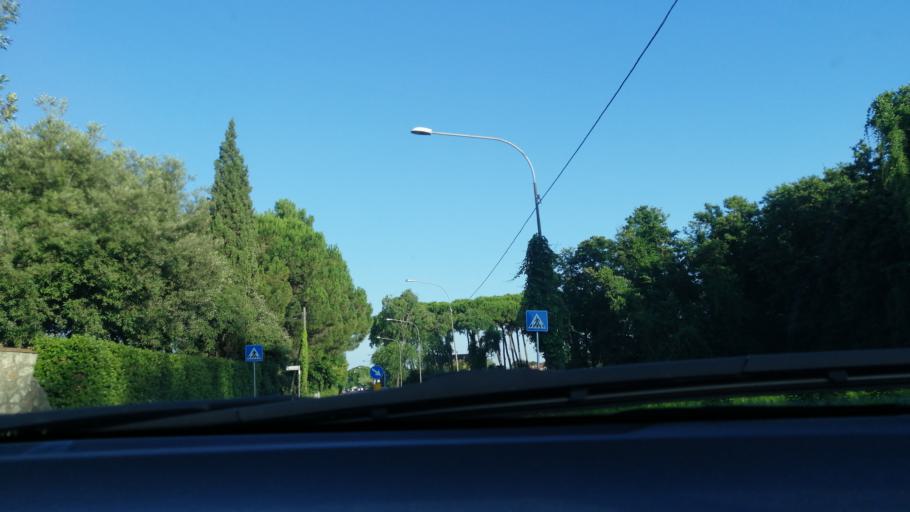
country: IT
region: Tuscany
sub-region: Provincia di Lucca
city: Pietrasanta
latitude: 43.9241
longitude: 10.2142
